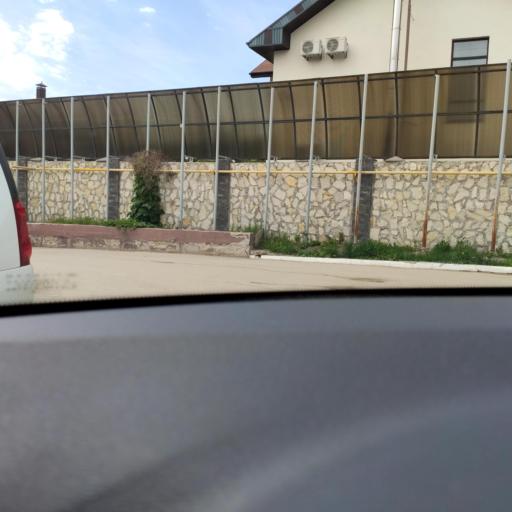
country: RU
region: Samara
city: Samara
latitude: 53.2897
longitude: 50.2215
